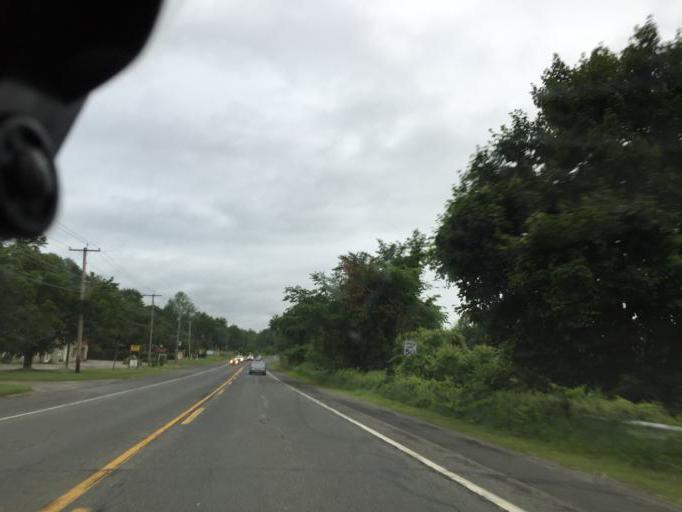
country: US
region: Massachusetts
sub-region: Berkshire County
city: Sheffield
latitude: 42.1247
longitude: -73.3587
